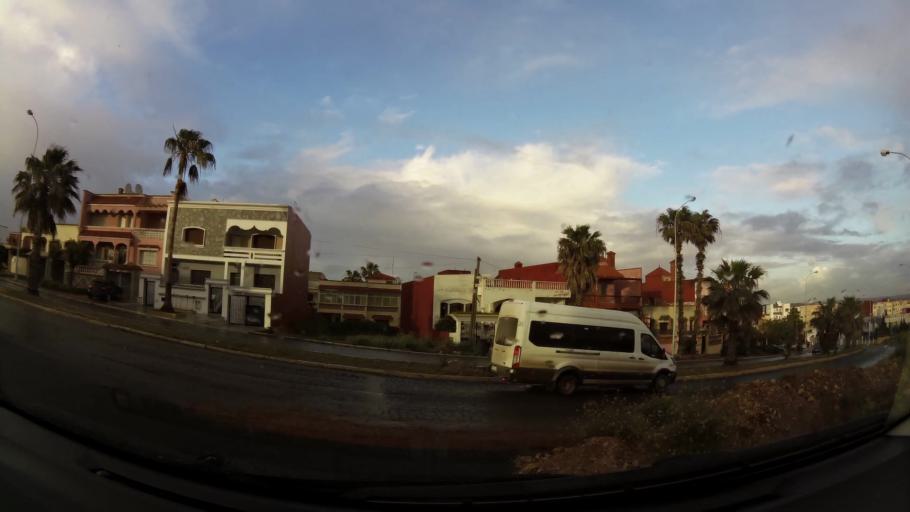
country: MA
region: Doukkala-Abda
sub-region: El-Jadida
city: El Jadida
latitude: 33.2288
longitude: -8.4964
